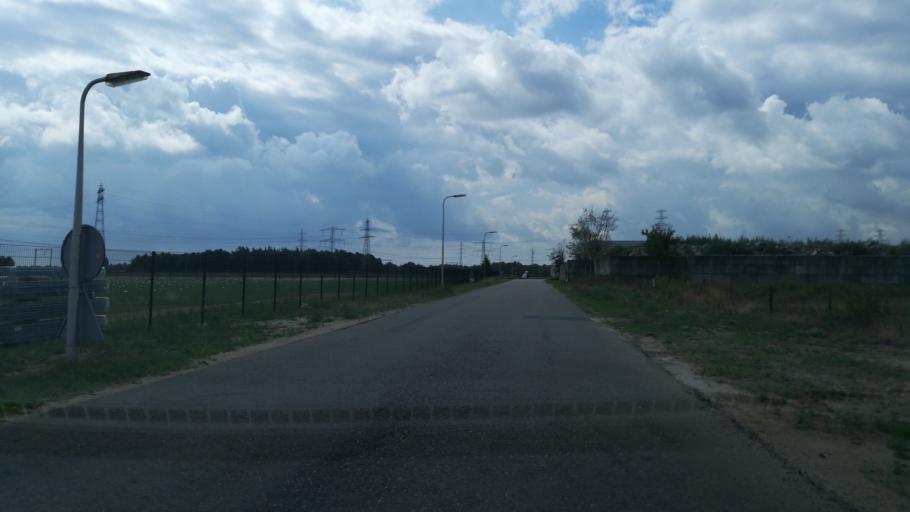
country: NL
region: Overijssel
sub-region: Gemeente Dalfsen
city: Dalfsen
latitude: 52.5322
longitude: 6.1824
